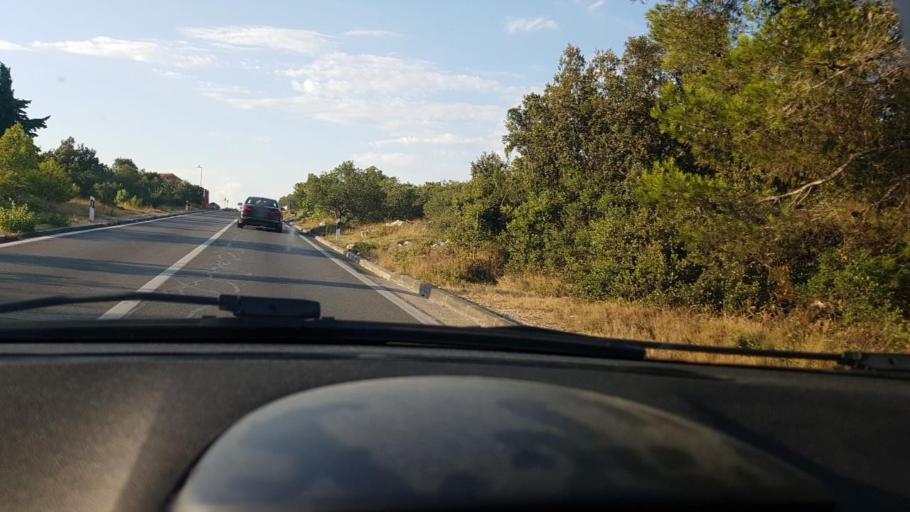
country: HR
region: Sibensko-Kniniska
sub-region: Grad Sibenik
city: Tisno
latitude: 43.7913
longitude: 15.6328
